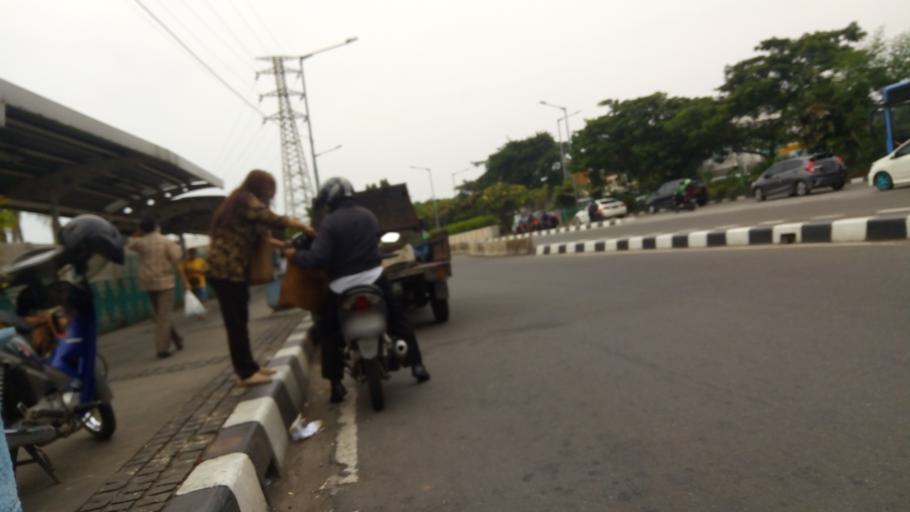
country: ID
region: Jakarta Raya
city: Jakarta
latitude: -6.1779
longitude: 106.8425
